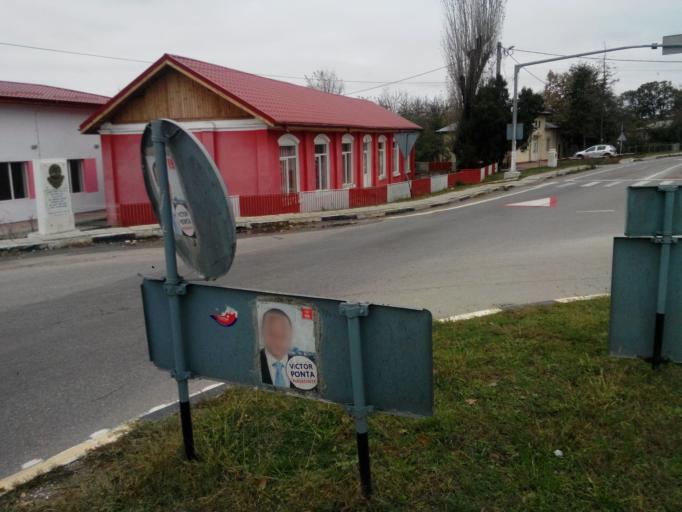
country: RO
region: Giurgiu
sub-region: Comuna Calugareni
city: Calugareni
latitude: 44.1719
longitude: 25.9963
